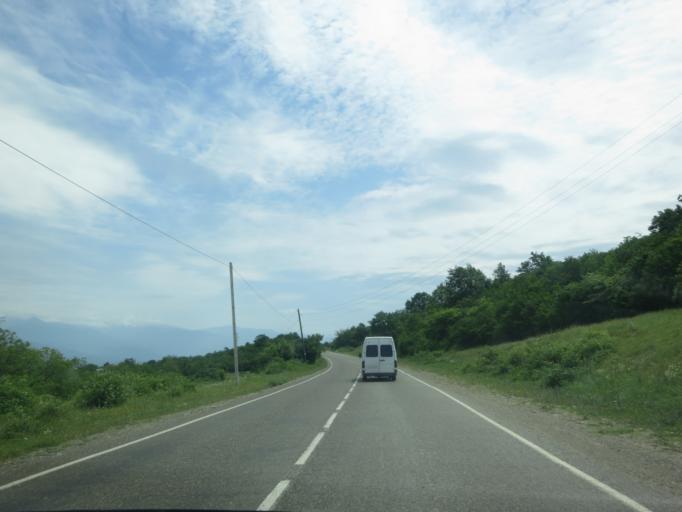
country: GE
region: Kakheti
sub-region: Telavi
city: Telavi
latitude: 41.9282
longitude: 45.4213
